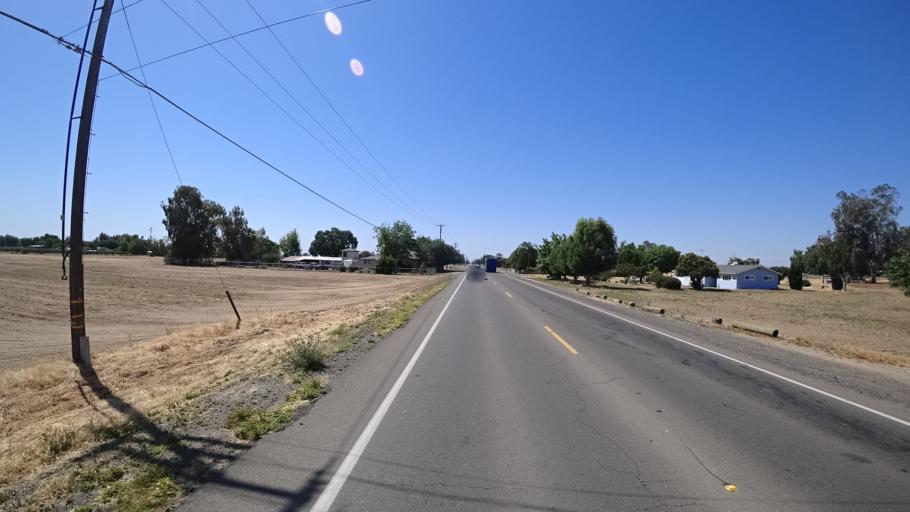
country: US
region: California
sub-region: Kings County
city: Lemoore
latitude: 36.2726
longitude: -119.7809
